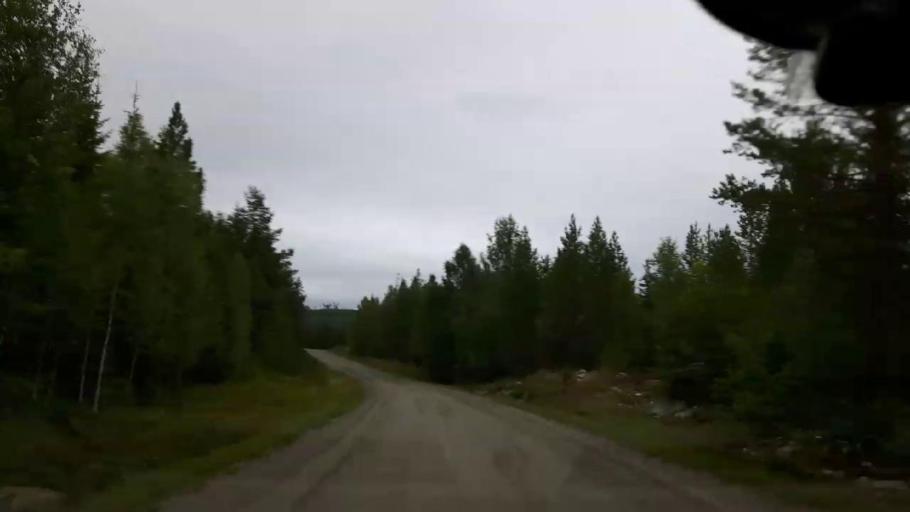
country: SE
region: Vaesternorrland
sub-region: Ange Kommun
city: Fransta
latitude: 62.8574
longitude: 15.9811
